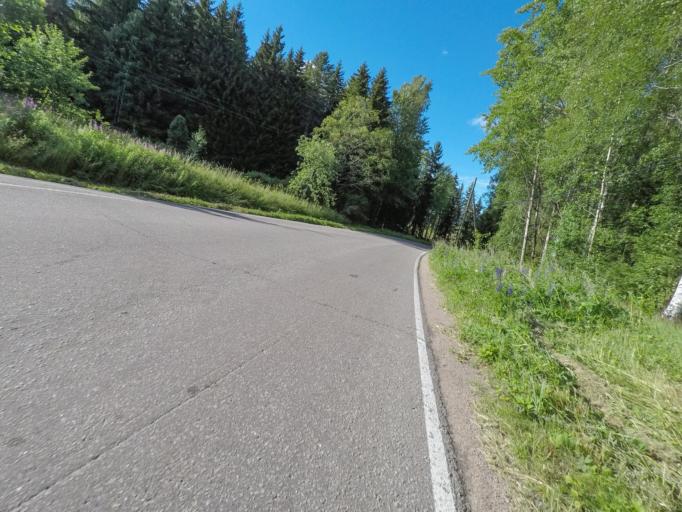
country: FI
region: South Karelia
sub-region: Imatra
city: Imatra
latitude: 61.1413
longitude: 28.7430
